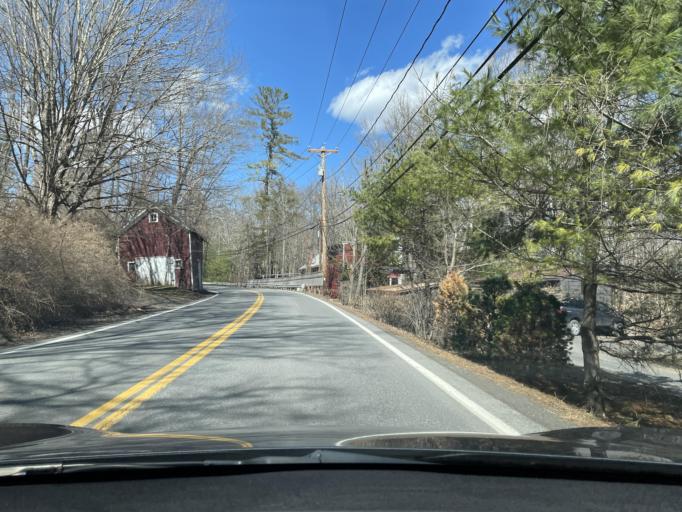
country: US
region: New York
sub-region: Ulster County
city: Zena
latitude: 42.0197
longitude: -74.0784
